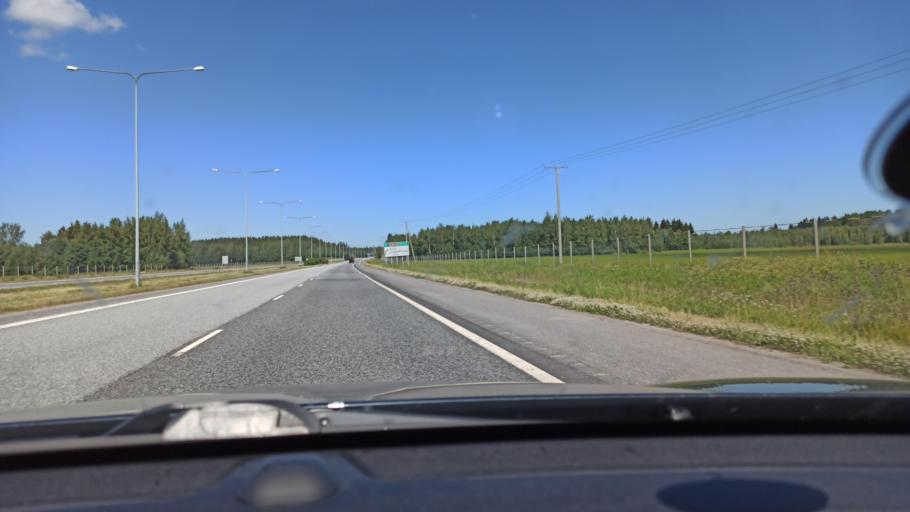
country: FI
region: Ostrobothnia
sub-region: Vaasa
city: Ristinummi
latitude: 63.0445
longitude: 21.7254
